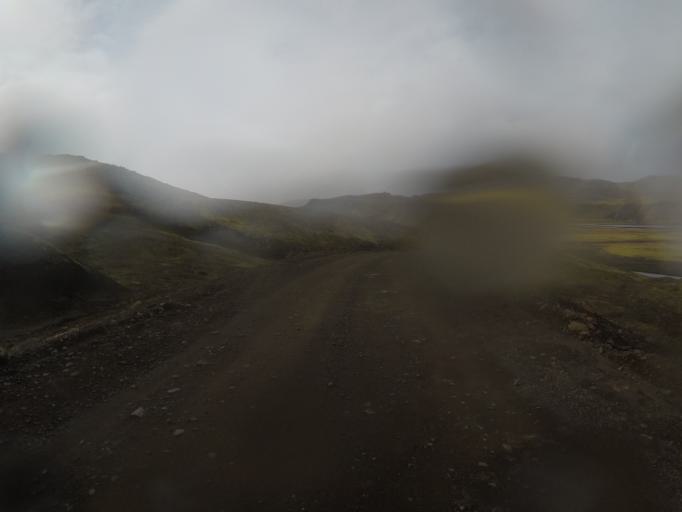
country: IS
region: South
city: Vestmannaeyjar
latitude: 63.9823
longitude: -18.8546
